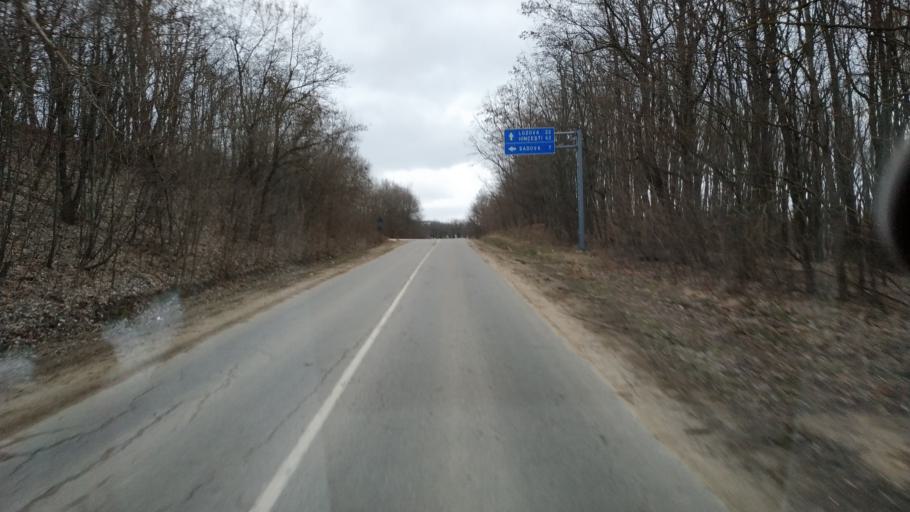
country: MD
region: Calarasi
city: Calarasi
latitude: 47.2231
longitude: 28.2747
